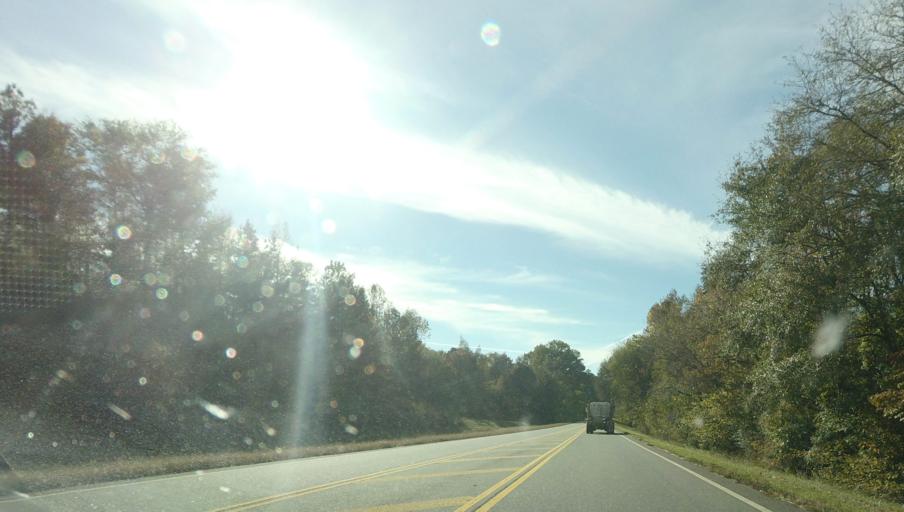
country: US
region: Georgia
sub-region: Talbot County
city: Talbotton
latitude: 32.6981
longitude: -84.4306
